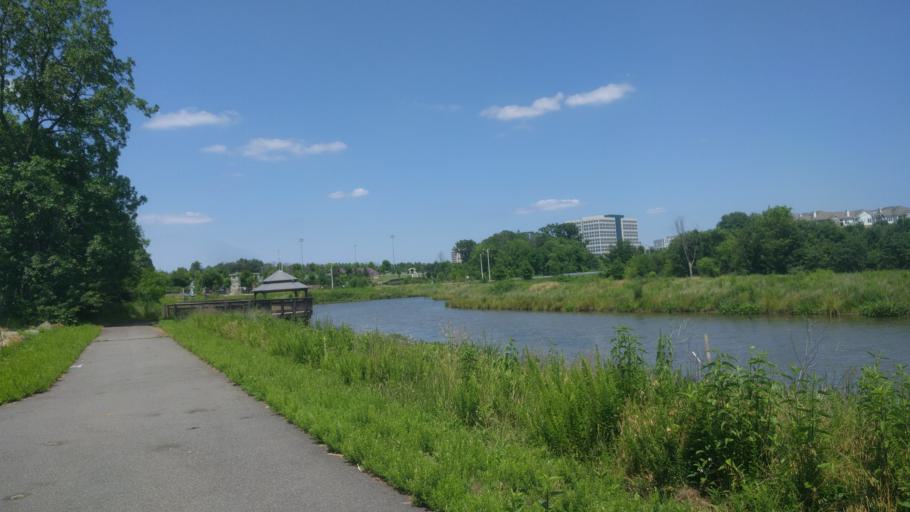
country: US
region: Virginia
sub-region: Fairfax County
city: Floris
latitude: 38.9516
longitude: -77.4122
